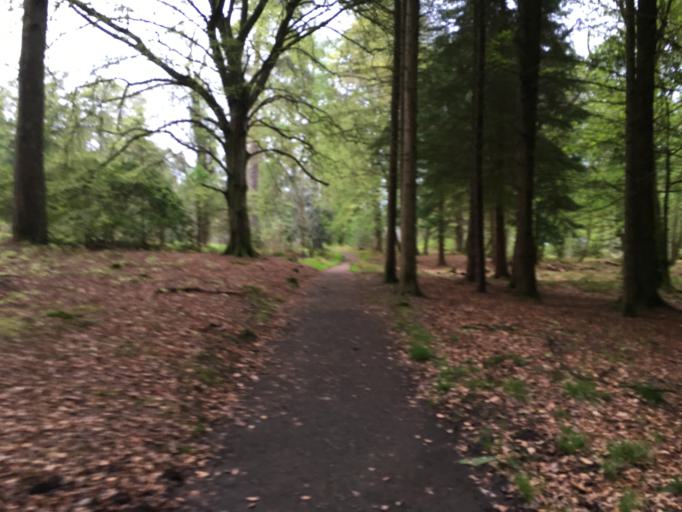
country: GB
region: Scotland
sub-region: Argyll and Bute
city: Rothesay
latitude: 55.7983
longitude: -5.0198
